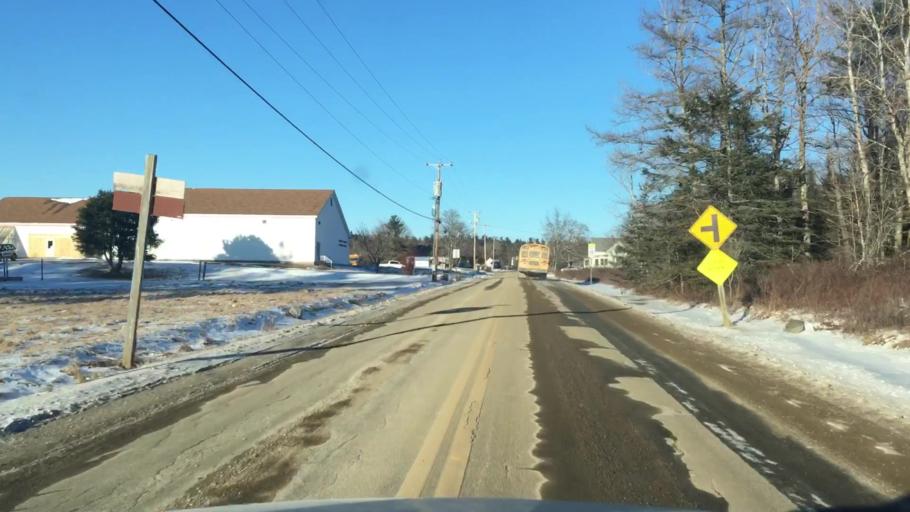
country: US
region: Maine
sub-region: Hancock County
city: Penobscot
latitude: 44.4671
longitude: -68.7095
